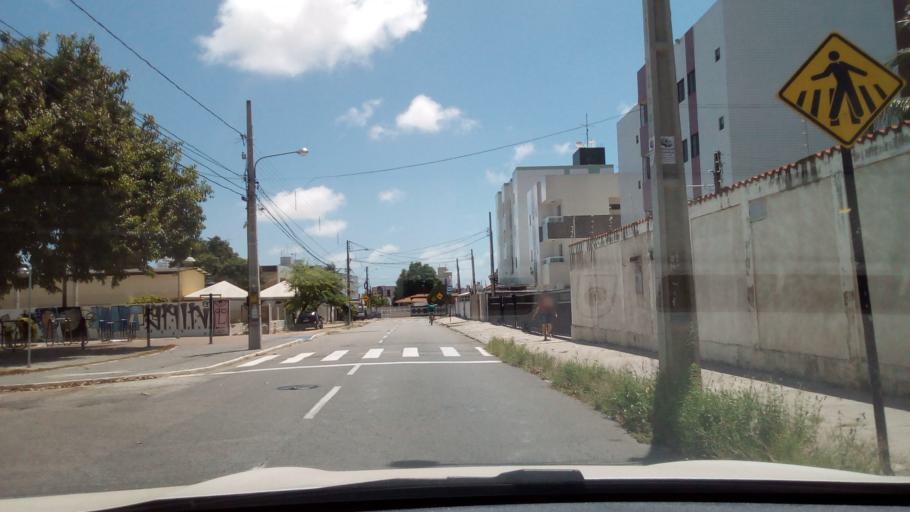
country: BR
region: Paraiba
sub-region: Joao Pessoa
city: Joao Pessoa
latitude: -7.1516
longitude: -34.8493
